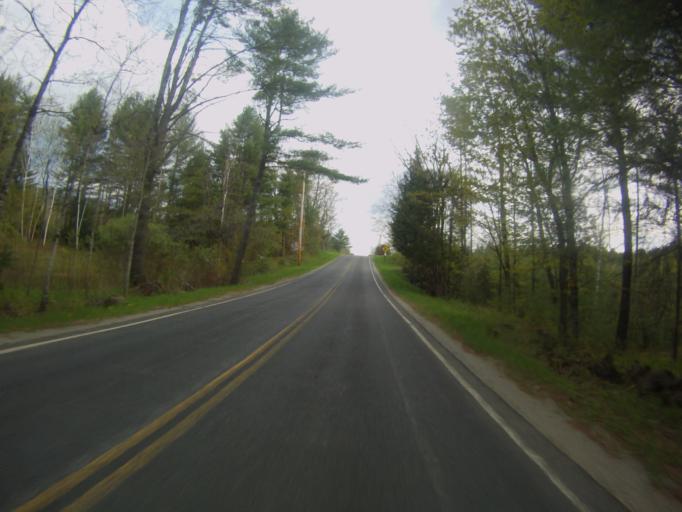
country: US
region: New York
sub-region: Warren County
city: Warrensburg
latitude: 43.8024
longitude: -73.9397
